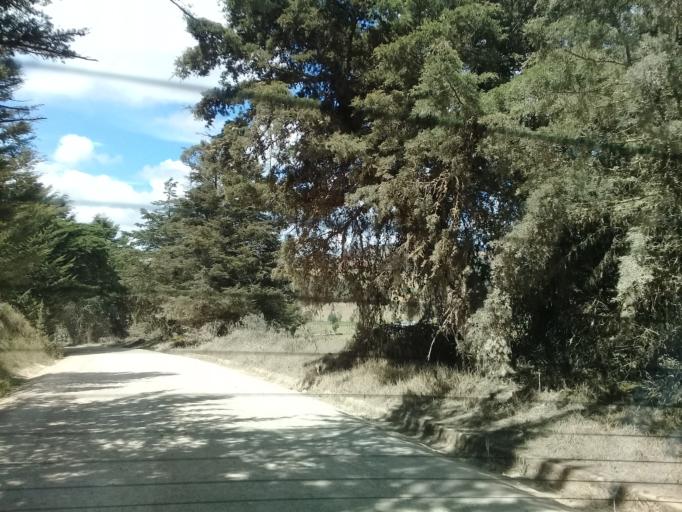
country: CO
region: Cundinamarca
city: Cucunuba
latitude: 5.1918
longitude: -73.7486
